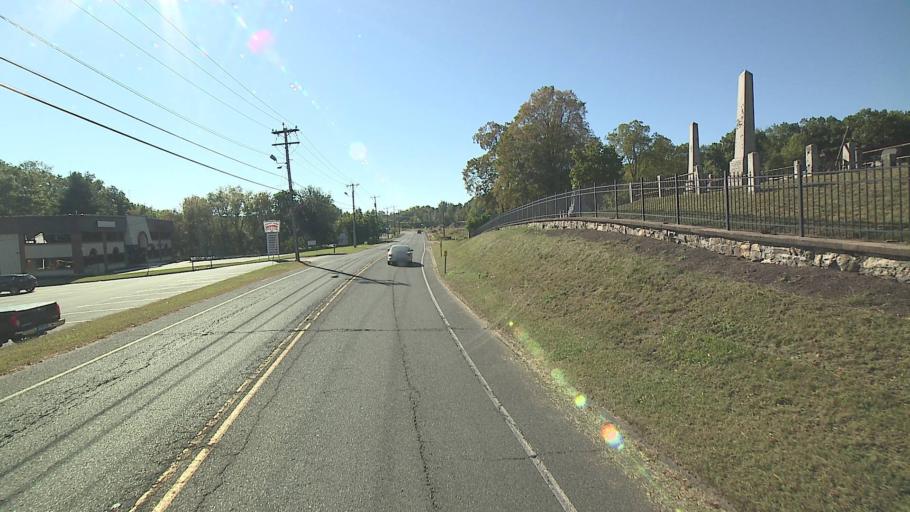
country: US
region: Connecticut
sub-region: Fairfield County
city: Danbury
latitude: 41.4611
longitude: -73.4069
